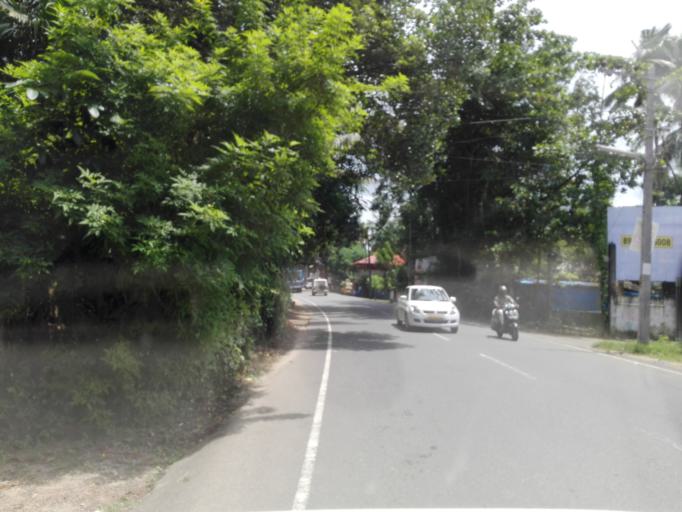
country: IN
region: Kerala
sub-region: Alappuzha
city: Arukutti
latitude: 9.8476
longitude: 76.3866
